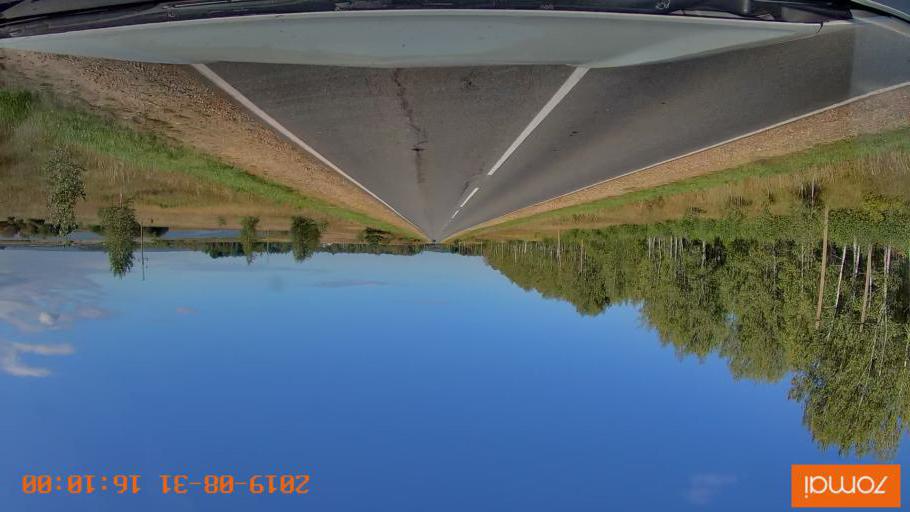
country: RU
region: Kaluga
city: Yukhnov
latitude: 54.5860
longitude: 35.4140
